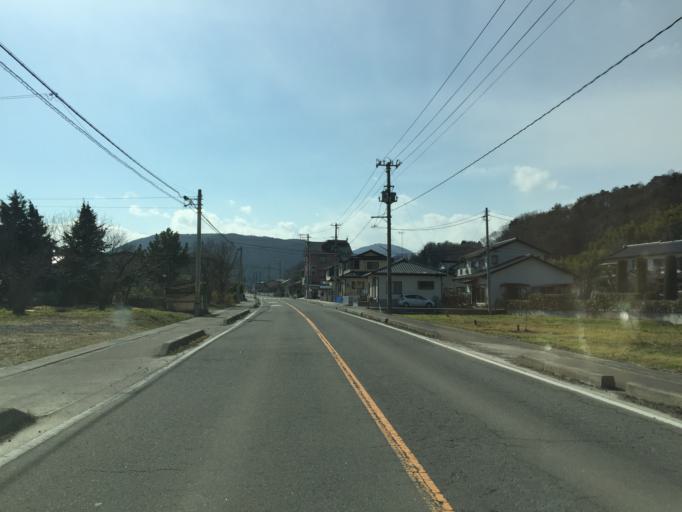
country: JP
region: Fukushima
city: Fukushima-shi
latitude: 37.8277
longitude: 140.4337
